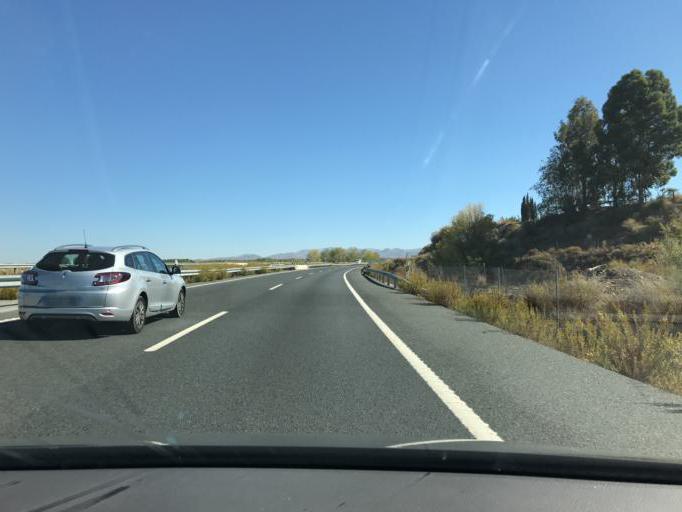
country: ES
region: Andalusia
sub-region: Provincia de Granada
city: Purullena
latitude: 37.3282
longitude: -3.1871
